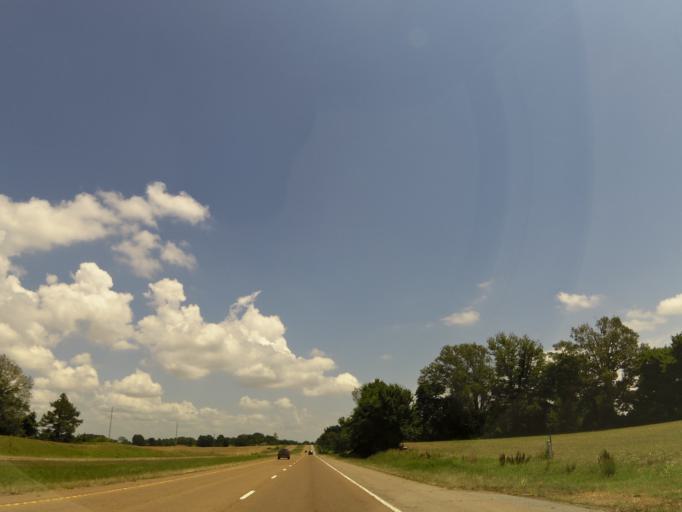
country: US
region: Tennessee
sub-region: Lauderdale County
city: Halls
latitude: 35.9441
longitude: -89.3034
